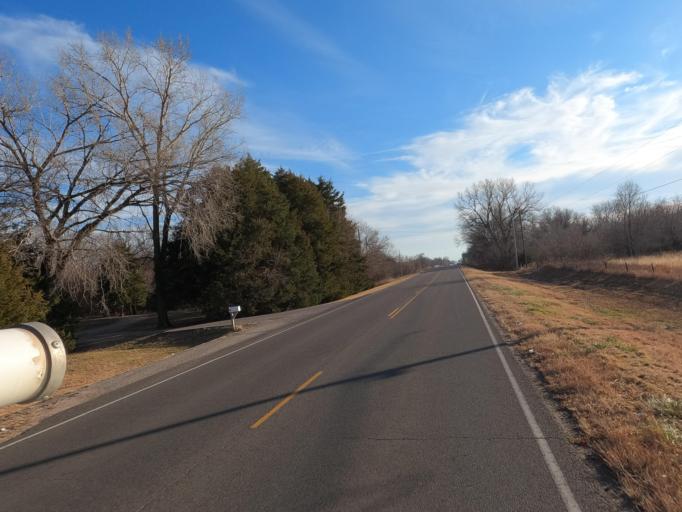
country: US
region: Kansas
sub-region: Reno County
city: Buhler
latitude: 38.1223
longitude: -97.7757
